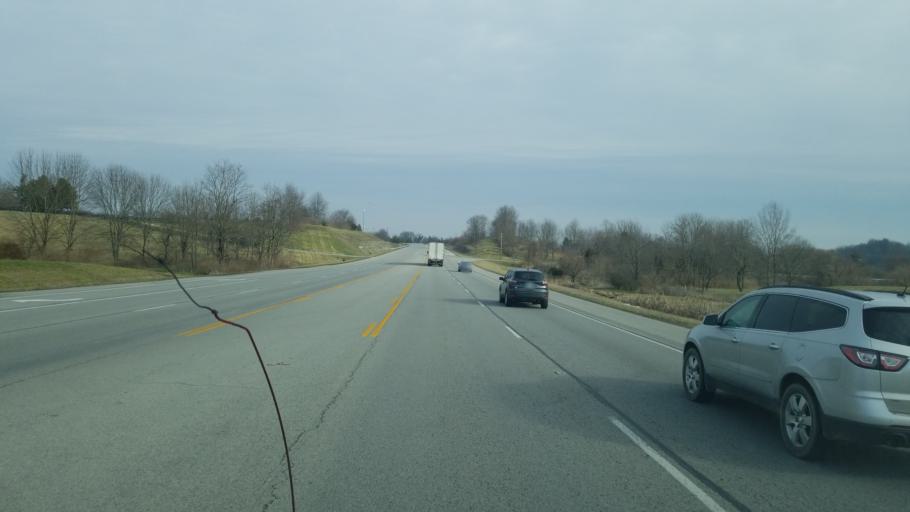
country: US
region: Kentucky
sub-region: Boyle County
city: Junction City
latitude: 37.5929
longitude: -84.7786
